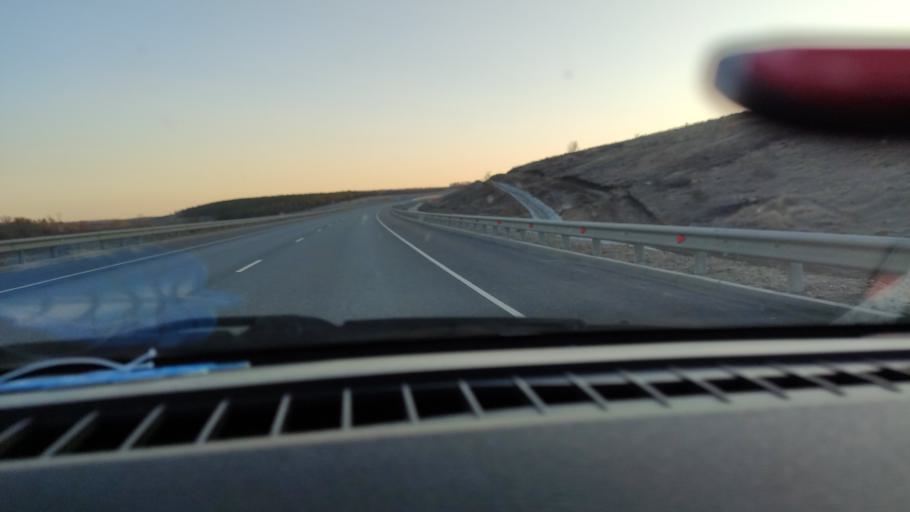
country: RU
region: Saratov
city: Yelshanka
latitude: 51.8728
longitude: 46.5045
